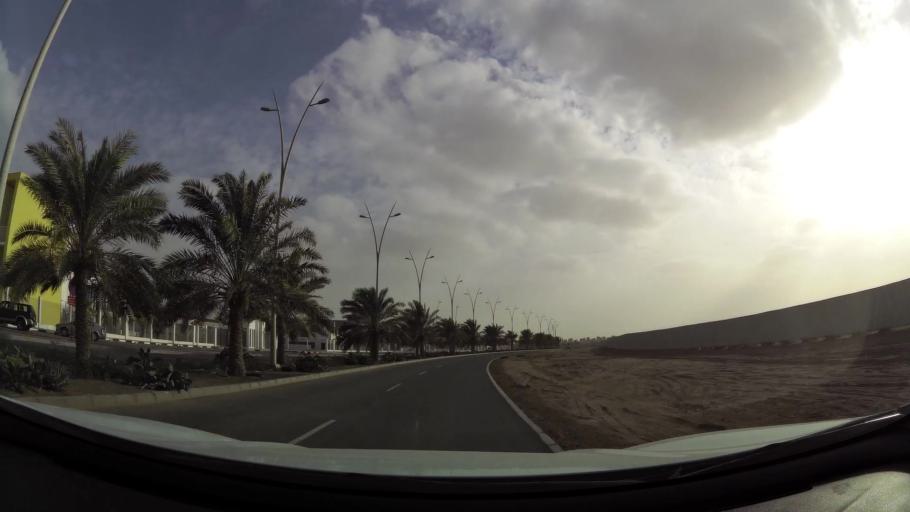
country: AE
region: Abu Dhabi
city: Abu Dhabi
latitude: 24.5091
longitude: 54.5994
